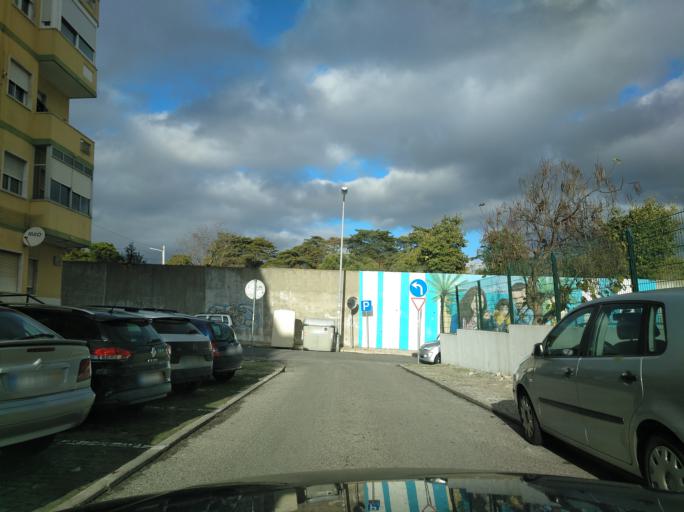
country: PT
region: Lisbon
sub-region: Loures
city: Sacavem
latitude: 38.7953
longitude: -9.1087
